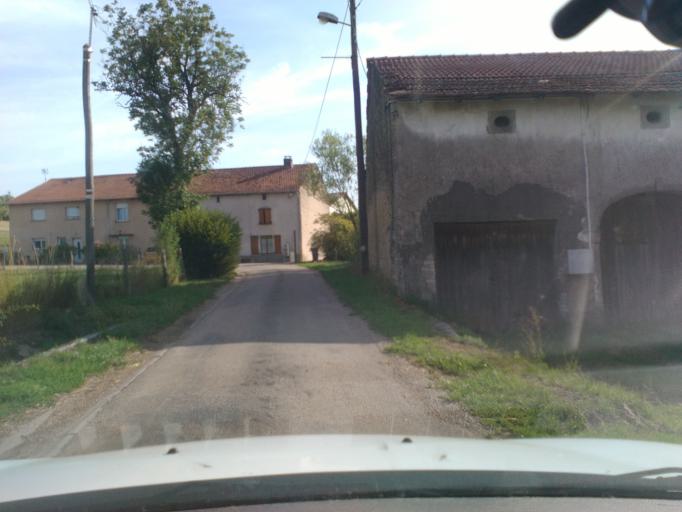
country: FR
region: Lorraine
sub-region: Departement des Vosges
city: Mirecourt
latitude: 48.3093
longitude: 6.0844
